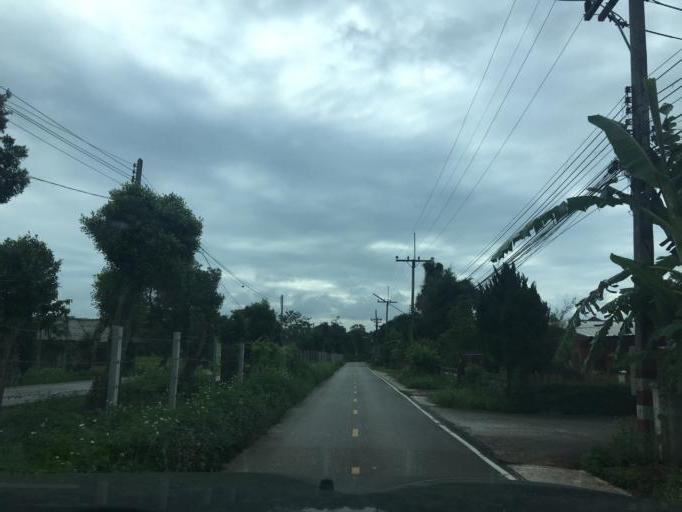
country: TH
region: Chiang Rai
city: Chiang Rai
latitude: 19.9993
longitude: 99.8633
